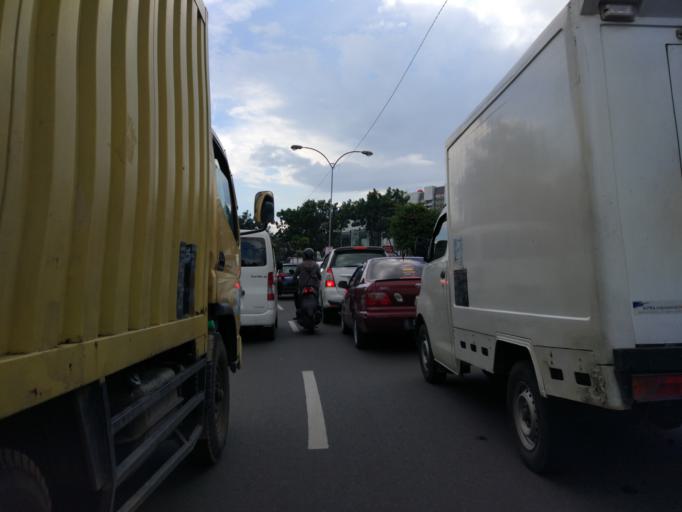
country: ID
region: West Java
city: Bandung
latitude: -6.9233
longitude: 107.6284
